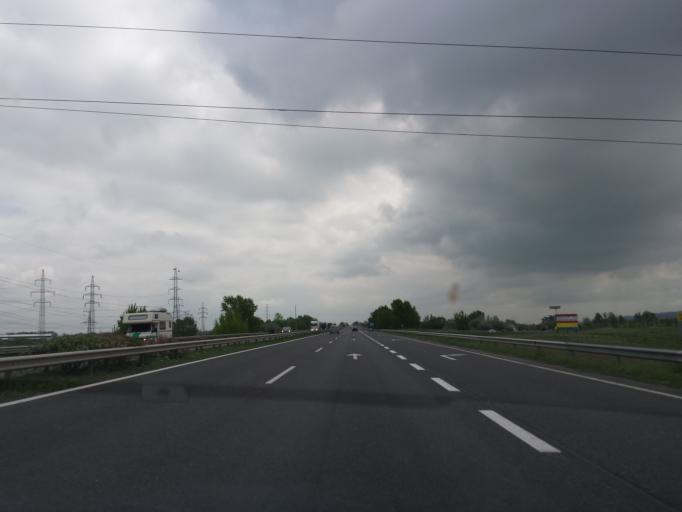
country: HU
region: Gyor-Moson-Sopron
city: Gyor
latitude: 47.6482
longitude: 17.6123
